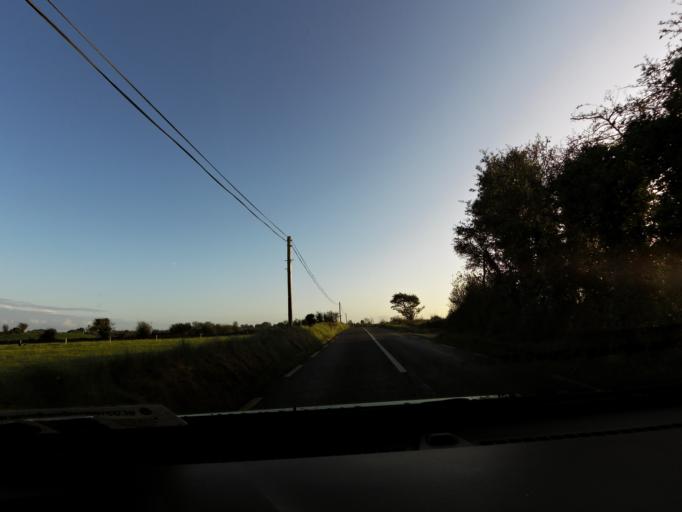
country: IE
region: Connaught
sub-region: Roscommon
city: Castlerea
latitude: 53.7078
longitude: -8.5649
